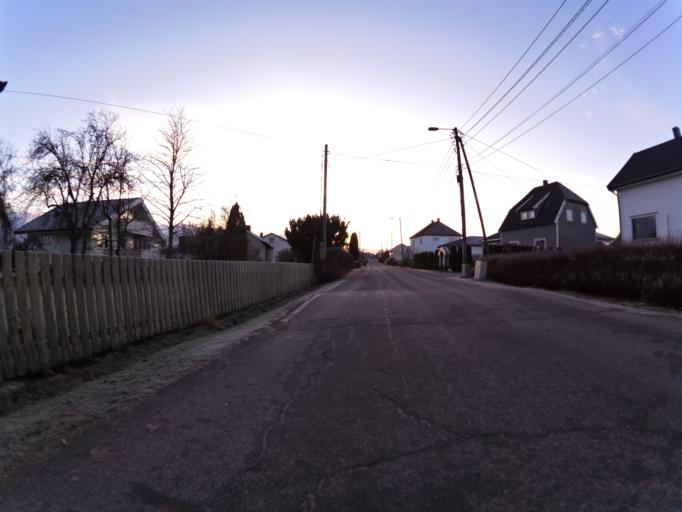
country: NO
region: Ostfold
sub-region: Sarpsborg
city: Sarpsborg
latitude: 59.2648
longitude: 11.0168
